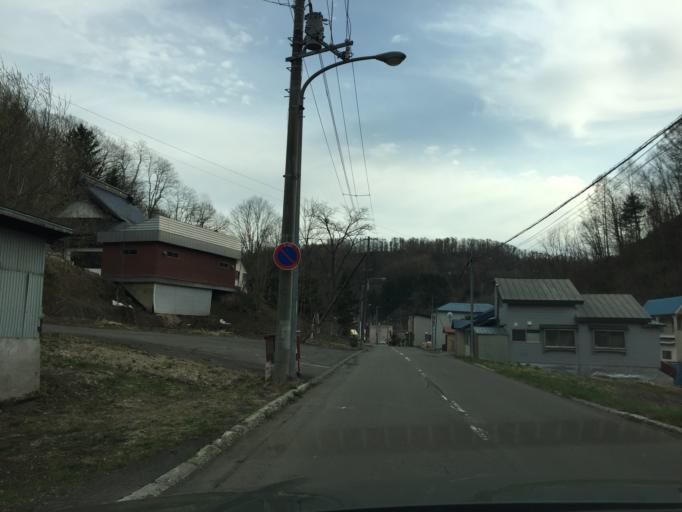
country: JP
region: Hokkaido
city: Utashinai
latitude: 43.5247
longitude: 142.0415
